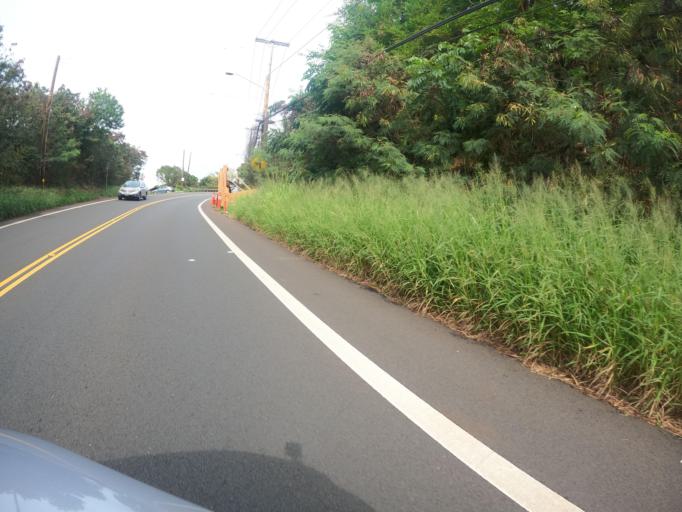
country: US
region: Hawaii
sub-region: Honolulu County
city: Halawa Heights
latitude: 21.3823
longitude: -157.9147
